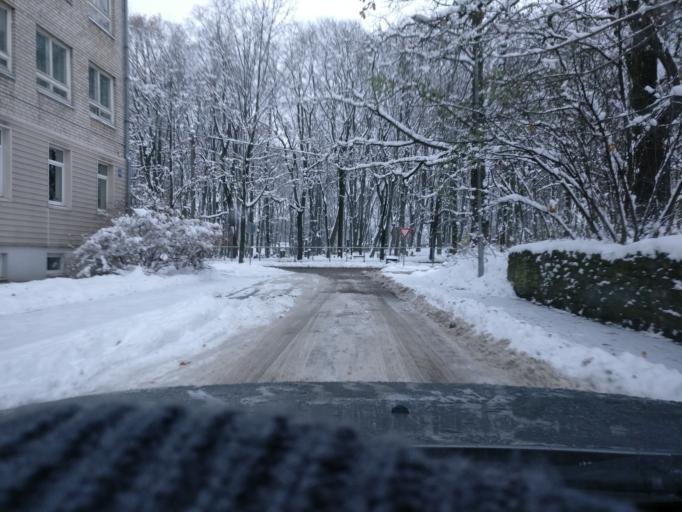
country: LV
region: Riga
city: Riga
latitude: 56.9274
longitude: 24.0879
